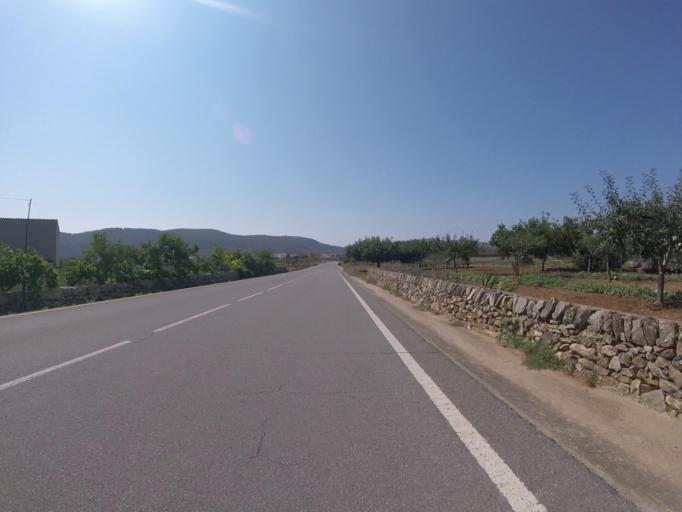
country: ES
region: Valencia
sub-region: Provincia de Castello
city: Adzaneta
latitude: 40.2259
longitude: -0.1733
